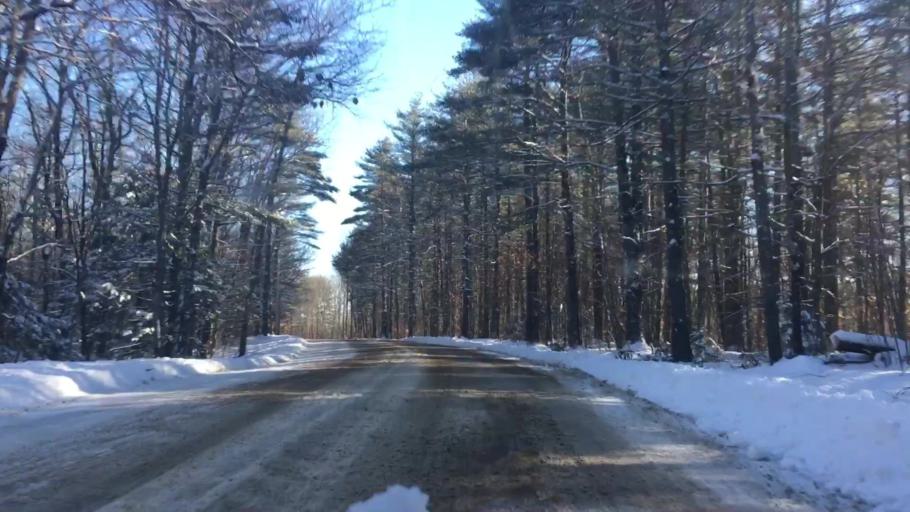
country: US
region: Maine
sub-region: Cumberland County
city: New Gloucester
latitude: 43.9641
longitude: -70.3450
